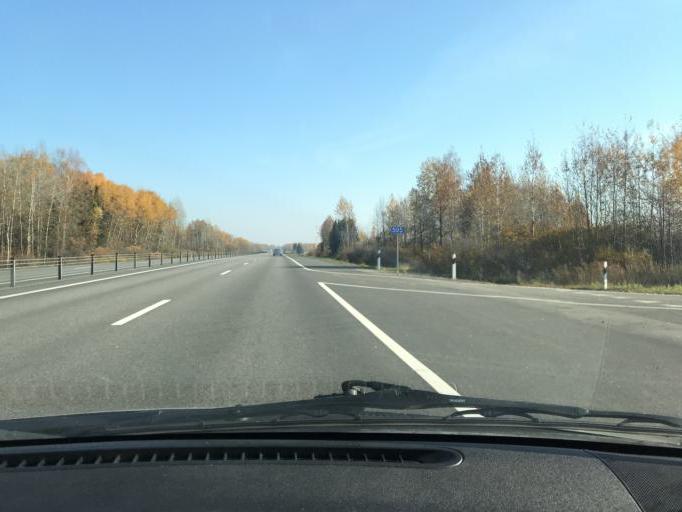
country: BY
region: Vitebsk
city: Dubrowna
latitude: 54.6782
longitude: 30.7521
